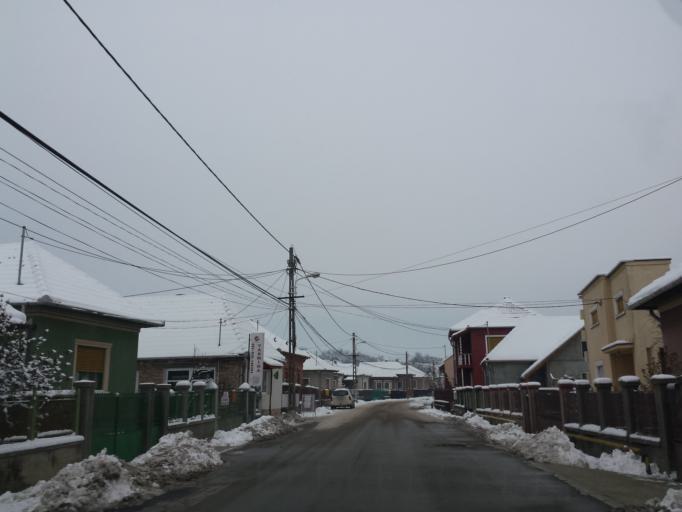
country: RO
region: Hunedoara
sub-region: Municipiul Deva
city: Cristur
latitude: 45.8276
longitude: 22.9413
